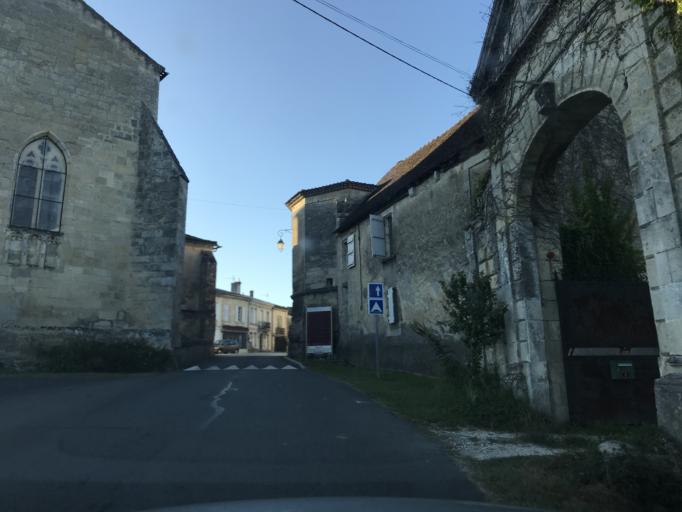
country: FR
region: Aquitaine
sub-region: Departement de la Gironde
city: Lussac
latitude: 44.9229
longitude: -0.0726
